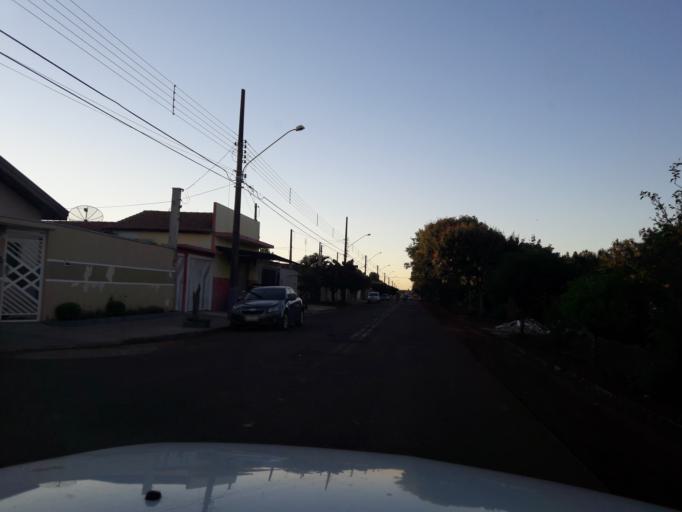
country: BR
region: Sao Paulo
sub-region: Moji-Guacu
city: Mogi-Gaucu
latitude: -22.3474
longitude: -46.9341
